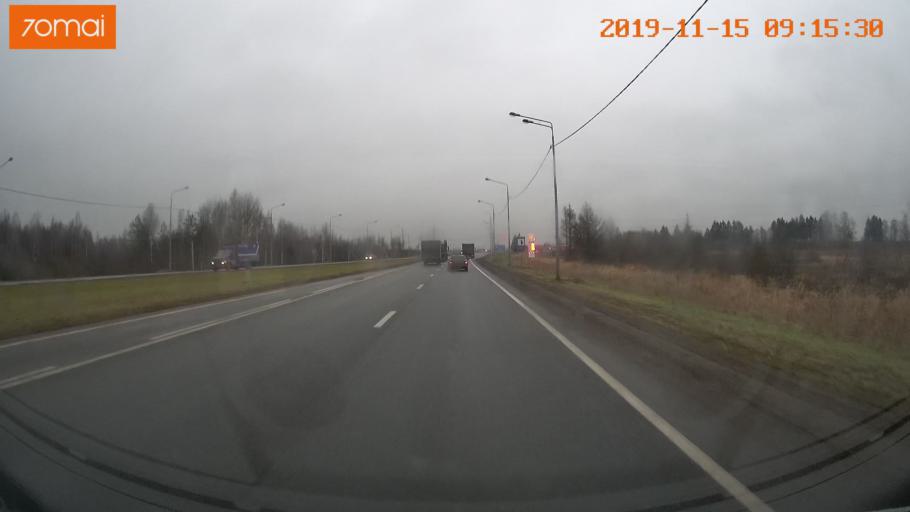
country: RU
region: Vologda
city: Tonshalovo
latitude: 59.2394
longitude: 37.9673
